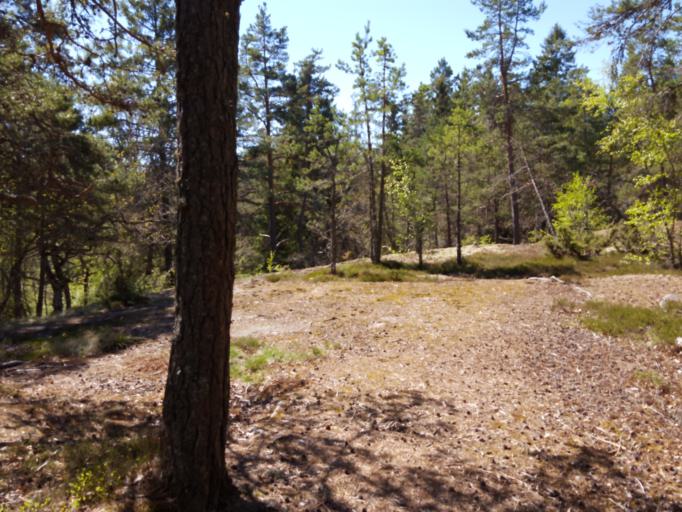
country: SE
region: Uppsala
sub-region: Uppsala Kommun
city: Storvreta
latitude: 59.9044
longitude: 17.7499
